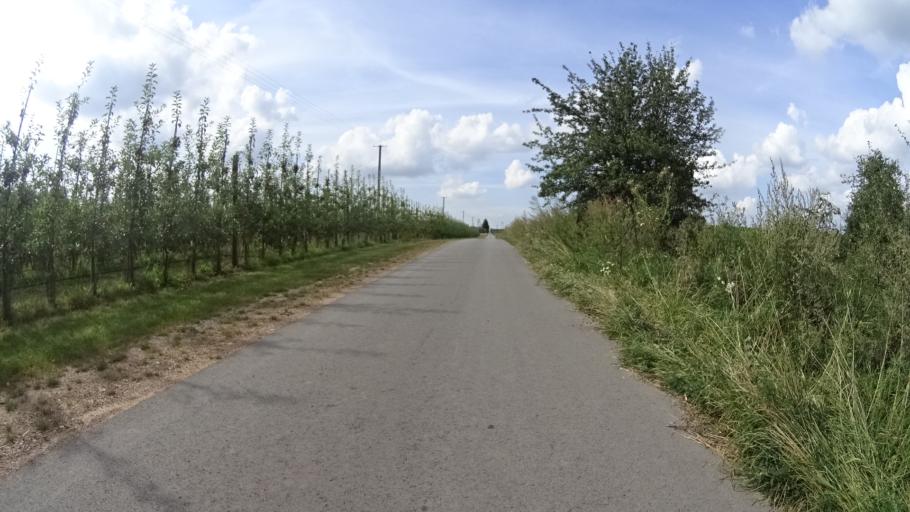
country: PL
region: Masovian Voivodeship
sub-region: Powiat grojecki
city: Goszczyn
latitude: 51.6975
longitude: 20.8199
